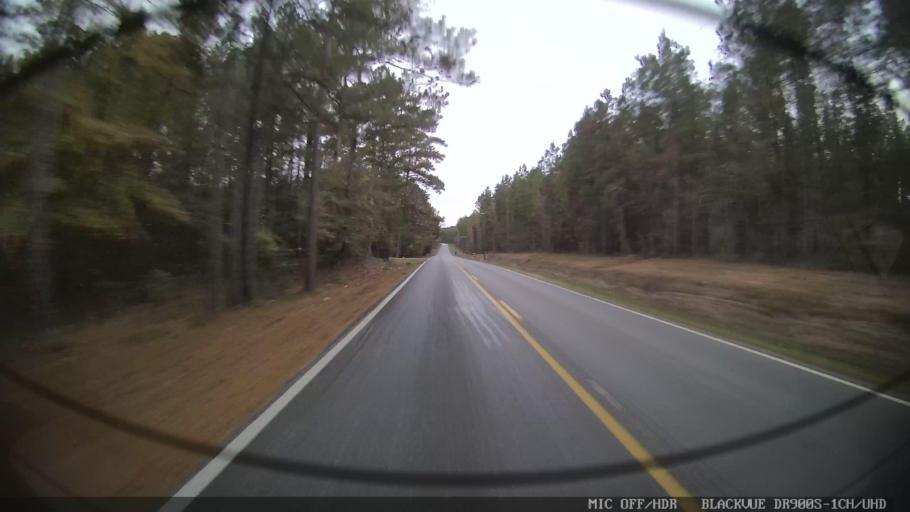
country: US
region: Mississippi
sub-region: Clarke County
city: Quitman
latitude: 32.0296
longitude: -88.8248
